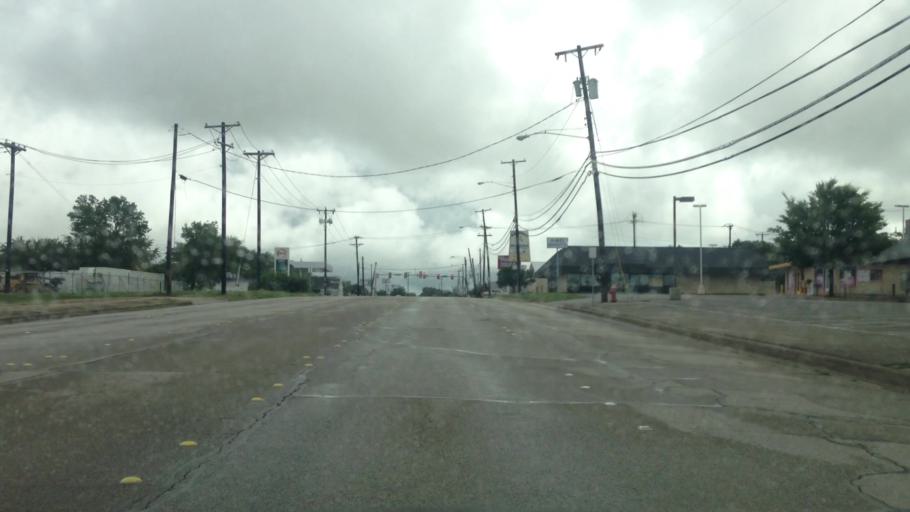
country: US
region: Texas
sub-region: Tarrant County
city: White Settlement
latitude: 32.7587
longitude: -97.4510
